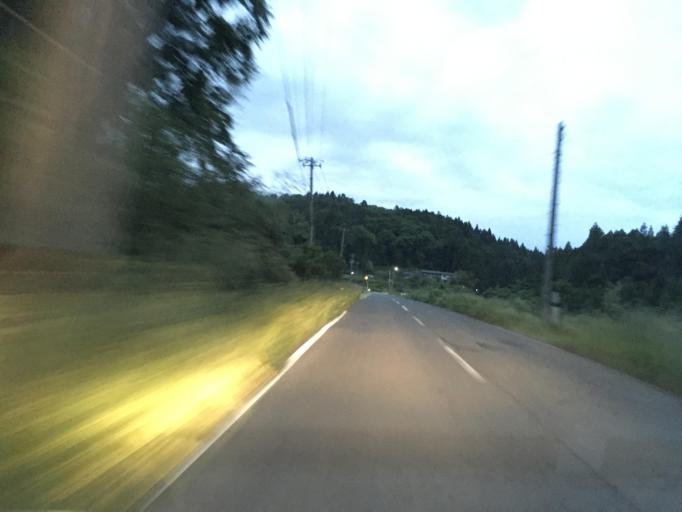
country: JP
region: Miyagi
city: Furukawa
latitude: 38.7664
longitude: 140.8793
